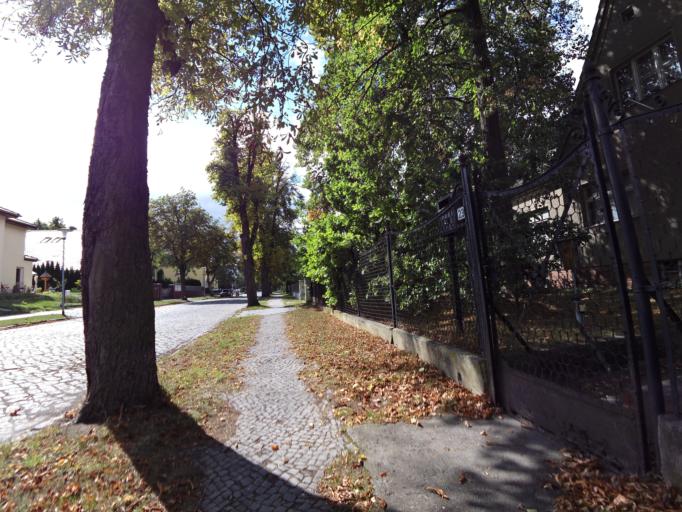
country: DE
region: Berlin
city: Lichtenrade
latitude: 52.3753
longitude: 13.3966
